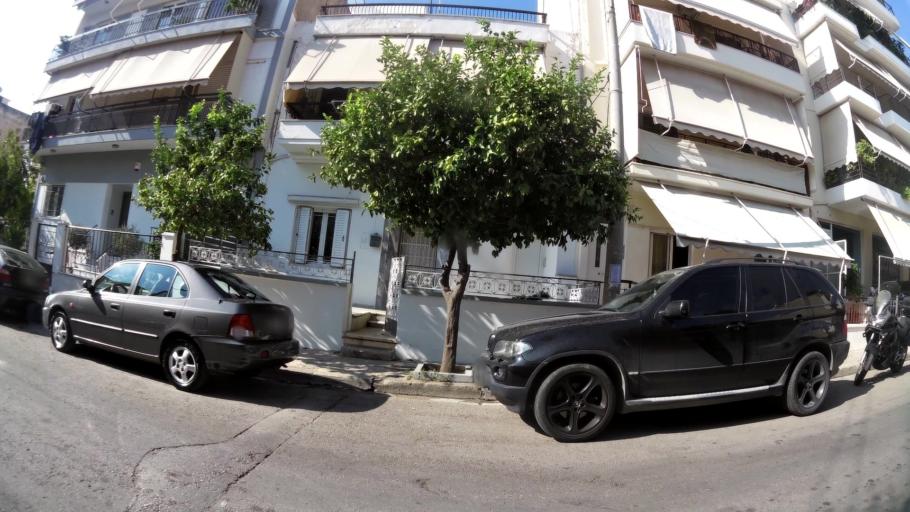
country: GR
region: Attica
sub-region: Nomos Piraios
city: Keratsini
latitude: 37.9674
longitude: 23.6202
